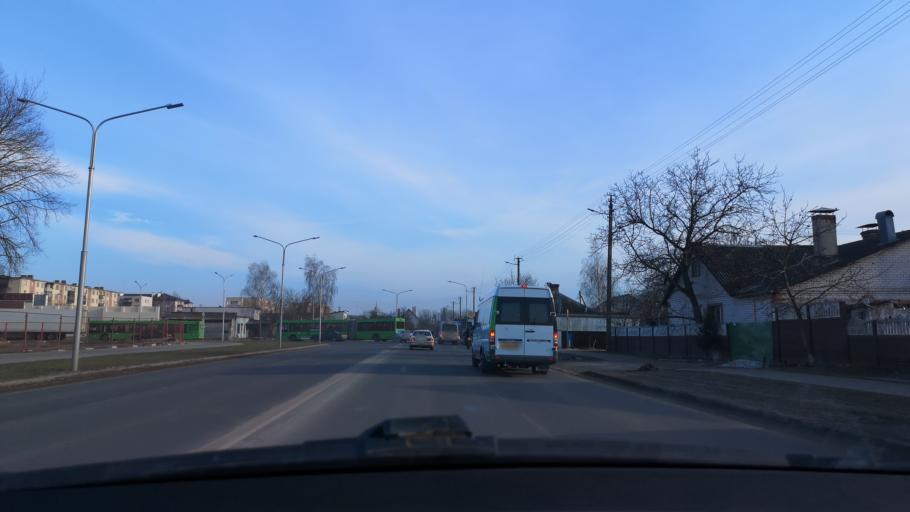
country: BY
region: Brest
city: Brest
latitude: 52.1034
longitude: 23.6690
